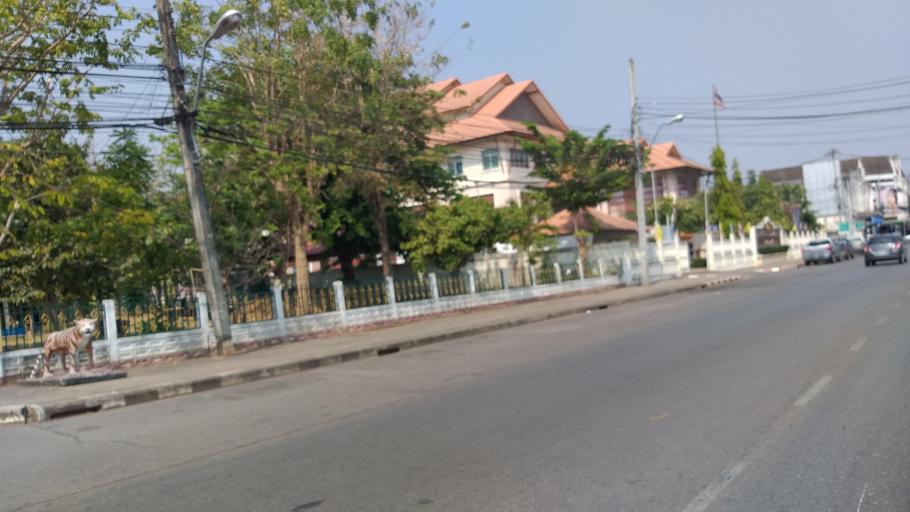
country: TH
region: Changwat Udon Thani
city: Udon Thani
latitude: 17.4049
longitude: 102.7847
